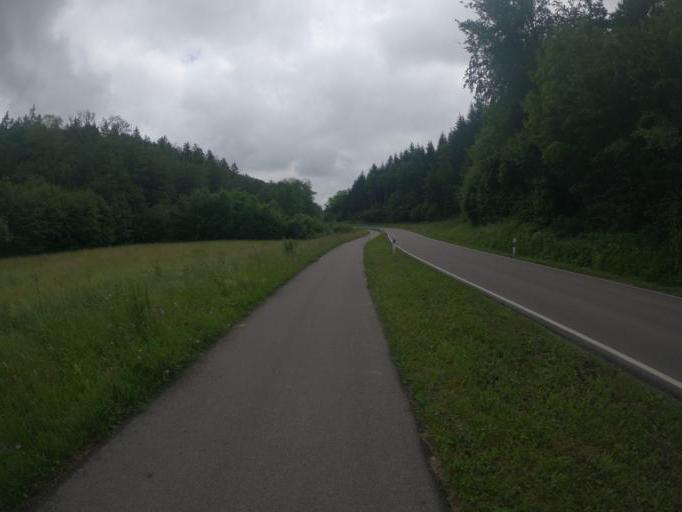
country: DE
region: Baden-Wuerttemberg
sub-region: Regierungsbezirk Stuttgart
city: Ebersbach an der Fils
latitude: 48.7330
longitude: 9.5522
